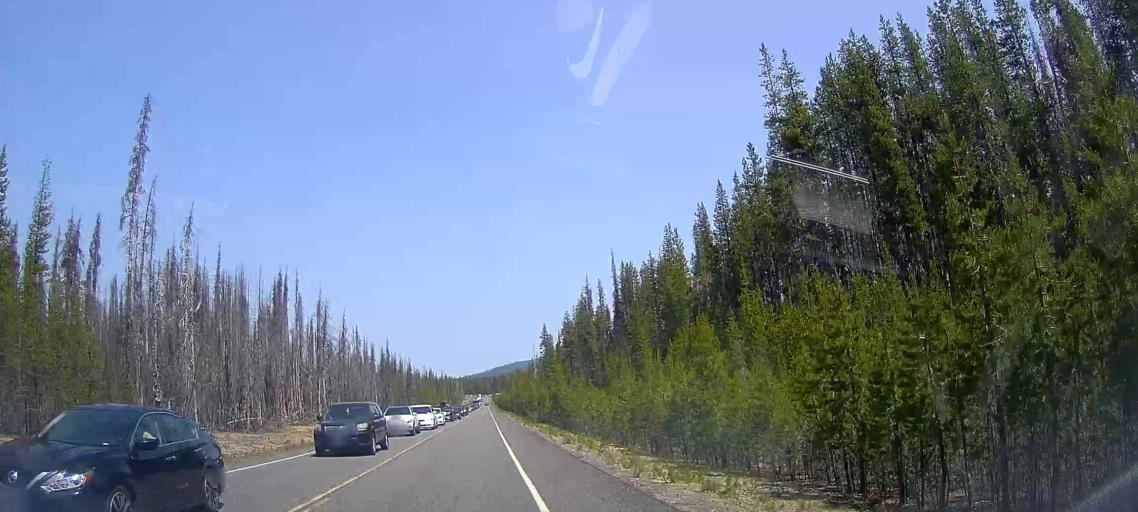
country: US
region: Oregon
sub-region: Lane County
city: Oakridge
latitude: 43.0807
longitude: -122.1174
